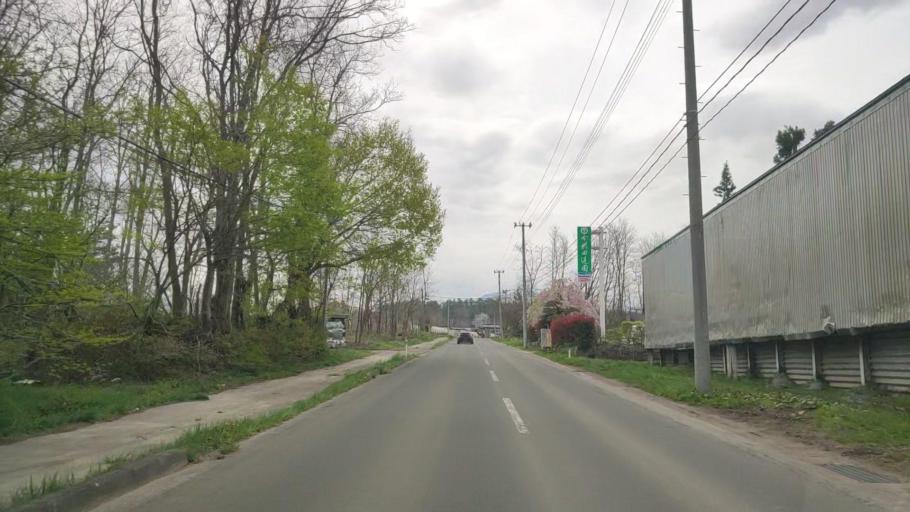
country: JP
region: Aomori
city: Aomori Shi
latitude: 40.7731
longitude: 140.7972
